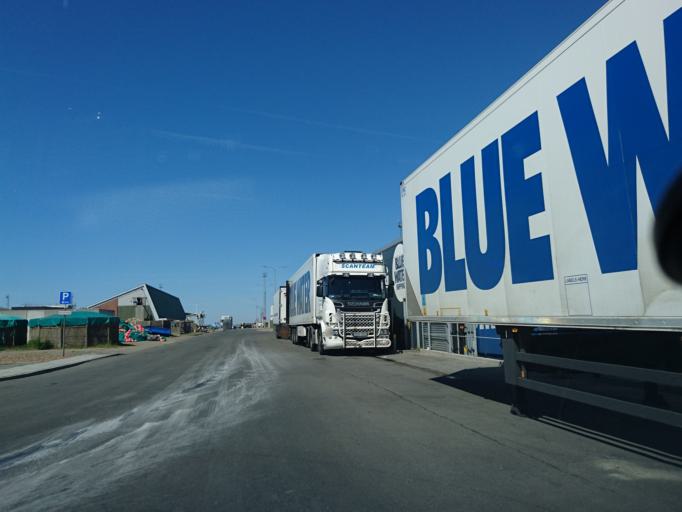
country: DK
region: North Denmark
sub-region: Hjorring Kommune
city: Hirtshals
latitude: 57.5926
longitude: 9.9781
